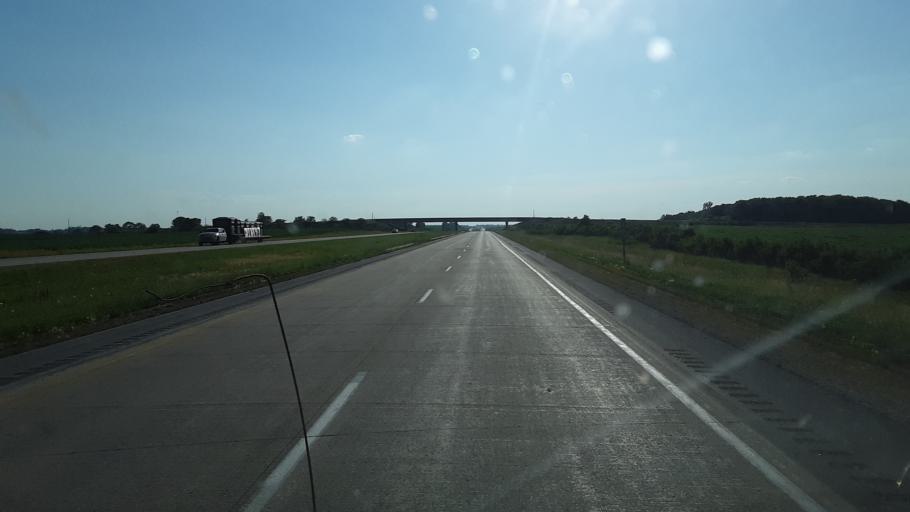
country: US
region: Iowa
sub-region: Hardin County
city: Iowa Falls
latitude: 42.4483
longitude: -93.2952
